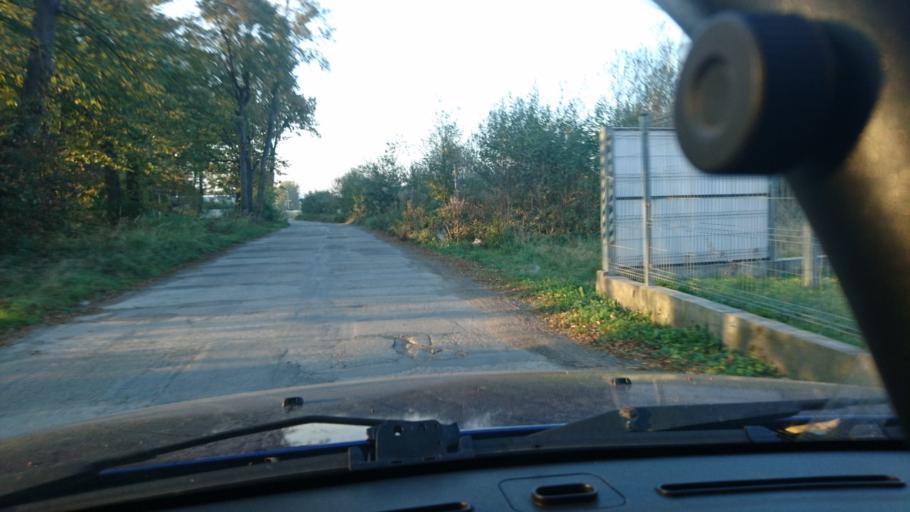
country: PL
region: Silesian Voivodeship
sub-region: Powiat bielski
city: Mazancowice
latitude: 49.8288
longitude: 18.9781
